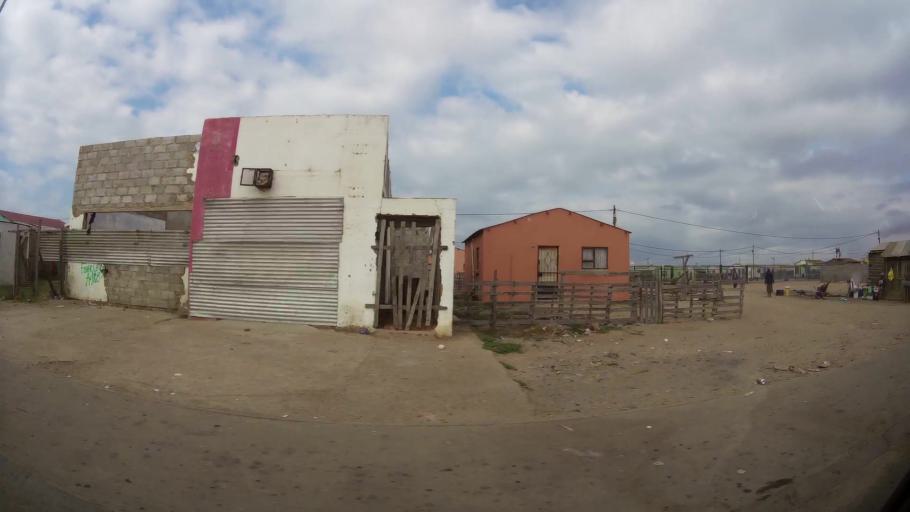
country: ZA
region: Eastern Cape
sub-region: Nelson Mandela Bay Metropolitan Municipality
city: Port Elizabeth
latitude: -33.8256
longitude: 25.6339
